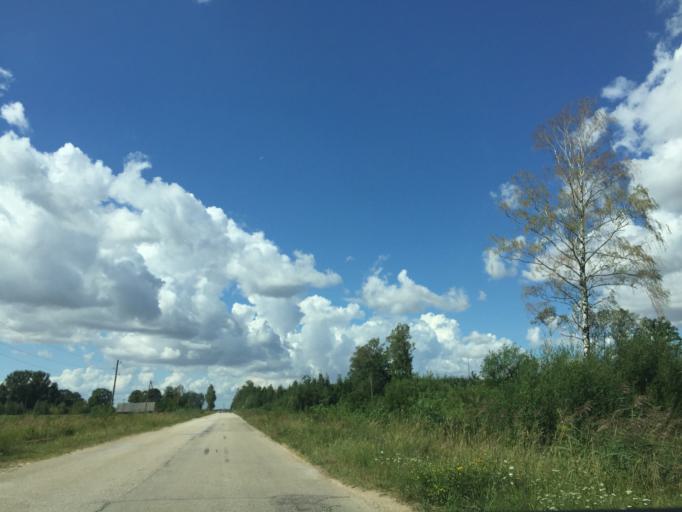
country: LV
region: Bauskas Rajons
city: Bauska
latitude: 56.3928
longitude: 24.1073
